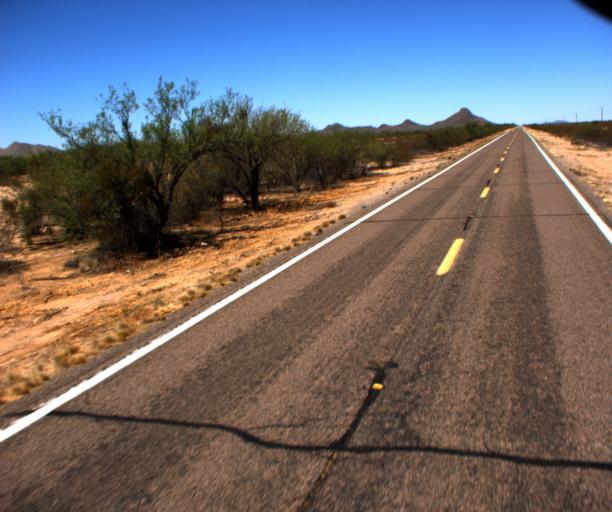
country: US
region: Arizona
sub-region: Pima County
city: Ajo
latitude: 32.1997
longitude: -112.4906
